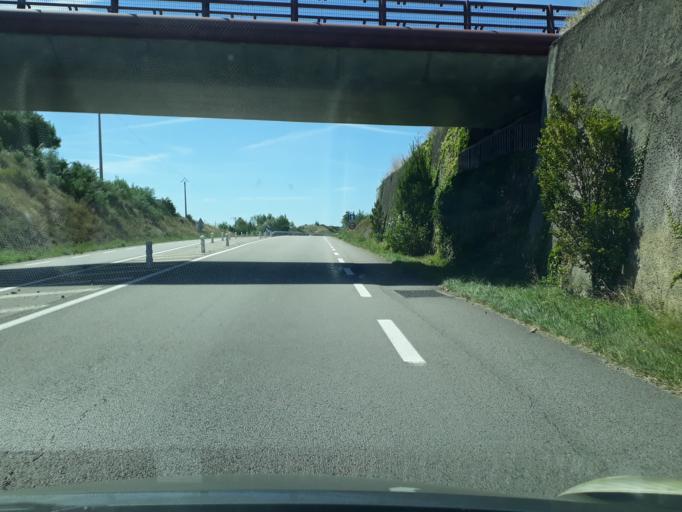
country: FR
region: Rhone-Alpes
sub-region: Departement de l'Ardeche
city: Peaugres
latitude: 45.2785
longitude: 4.7225
